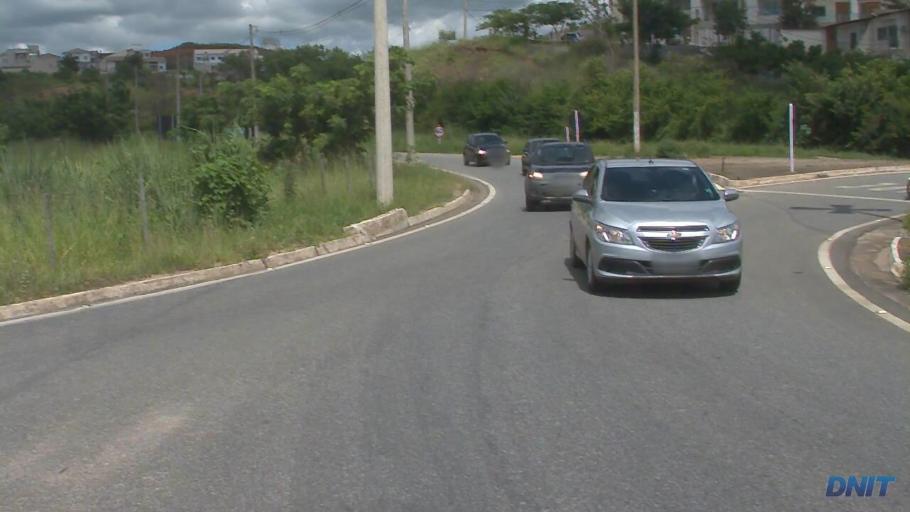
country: BR
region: Minas Gerais
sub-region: Governador Valadares
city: Governador Valadares
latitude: -18.8656
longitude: -41.9897
